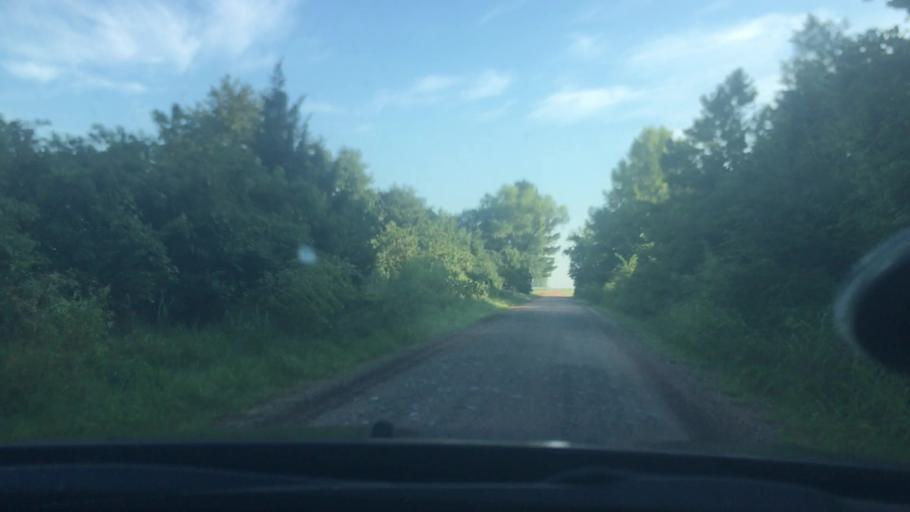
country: US
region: Oklahoma
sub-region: Pontotoc County
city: Ada
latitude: 34.8133
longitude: -96.7748
